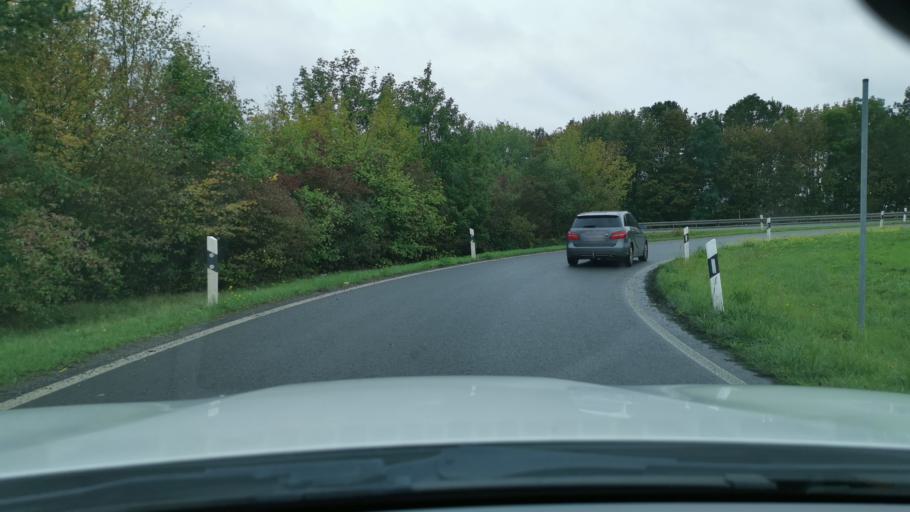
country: DE
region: Brandenburg
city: Wustermark
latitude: 52.5393
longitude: 12.9784
